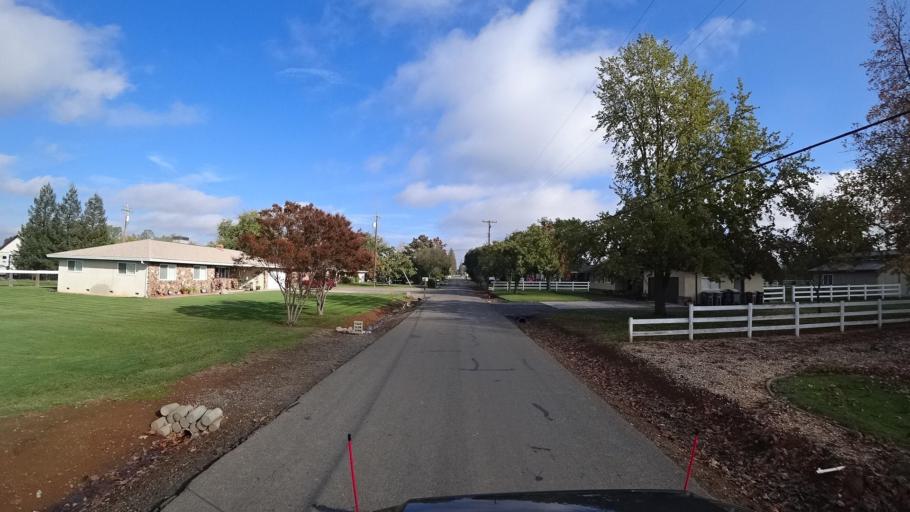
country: US
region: California
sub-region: Sacramento County
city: Vineyard
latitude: 38.4345
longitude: -121.3388
